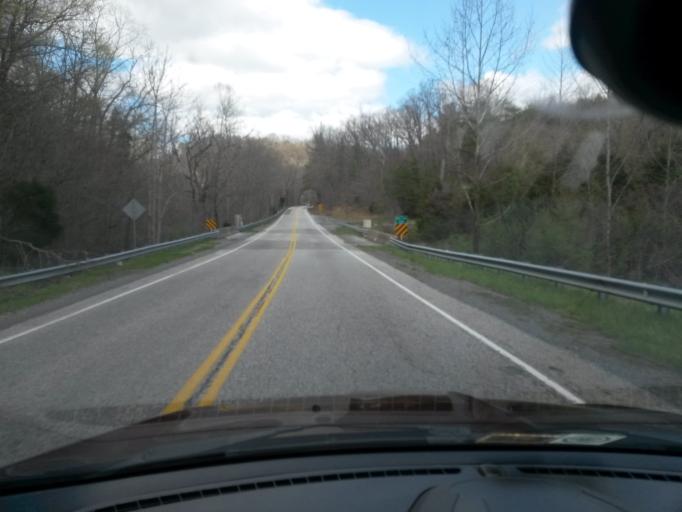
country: US
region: Virginia
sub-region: Rockbridge County
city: Glasgow
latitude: 37.6790
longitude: -79.4067
